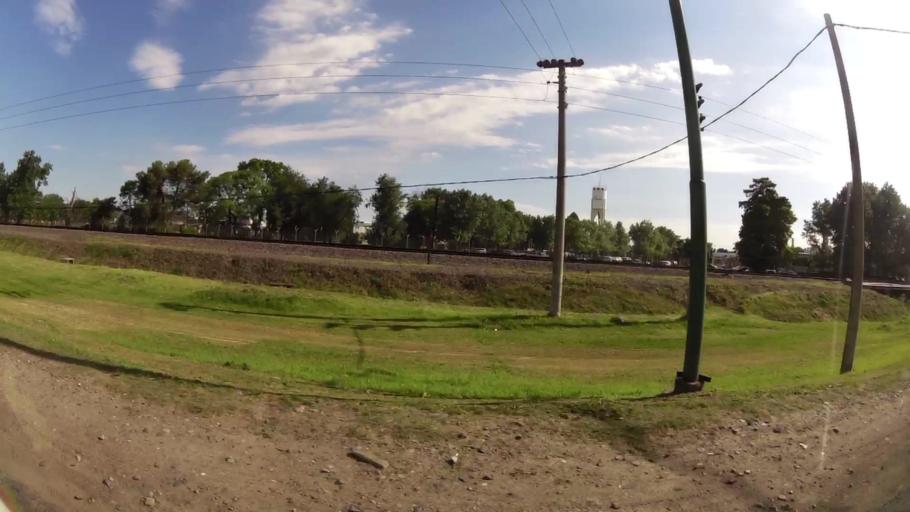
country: AR
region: Buenos Aires
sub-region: Partido de Merlo
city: Merlo
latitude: -34.6617
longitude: -58.7446
